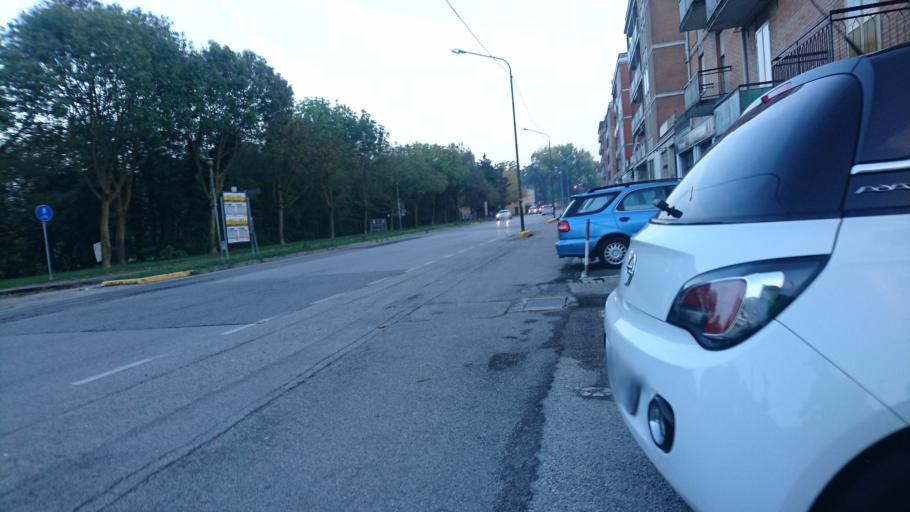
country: IT
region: Emilia-Romagna
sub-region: Provincia di Ferrara
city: Ferrara
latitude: 44.8525
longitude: 11.6151
